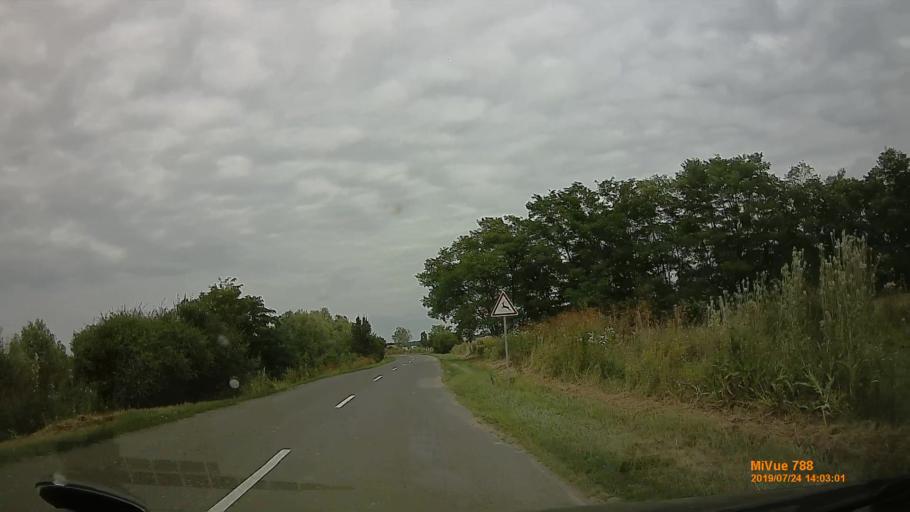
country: HU
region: Szabolcs-Szatmar-Bereg
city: Aranyosapati
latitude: 48.2740
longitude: 22.2847
